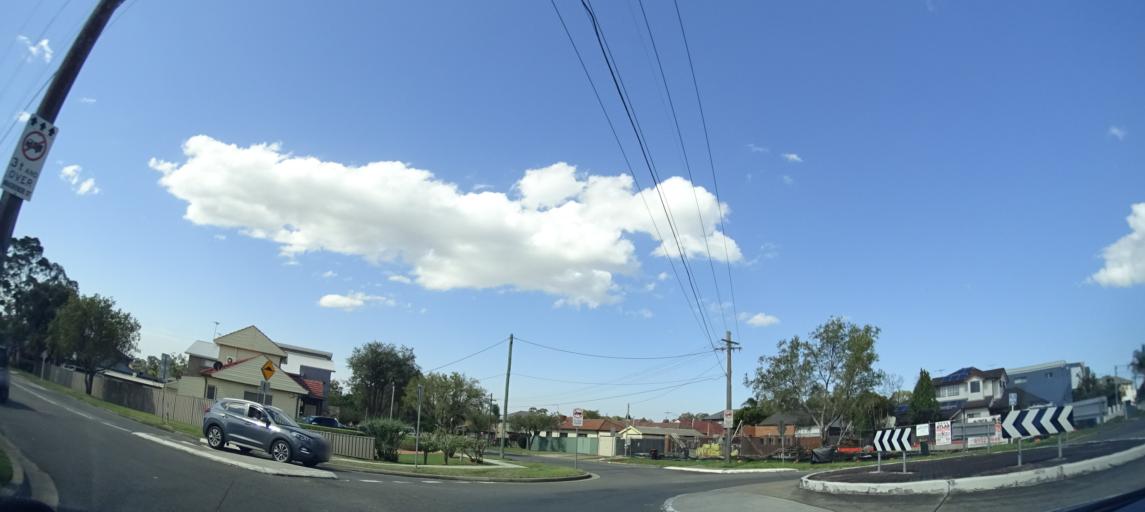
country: AU
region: New South Wales
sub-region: Bankstown
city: Revesby
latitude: -33.9472
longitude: 151.0224
